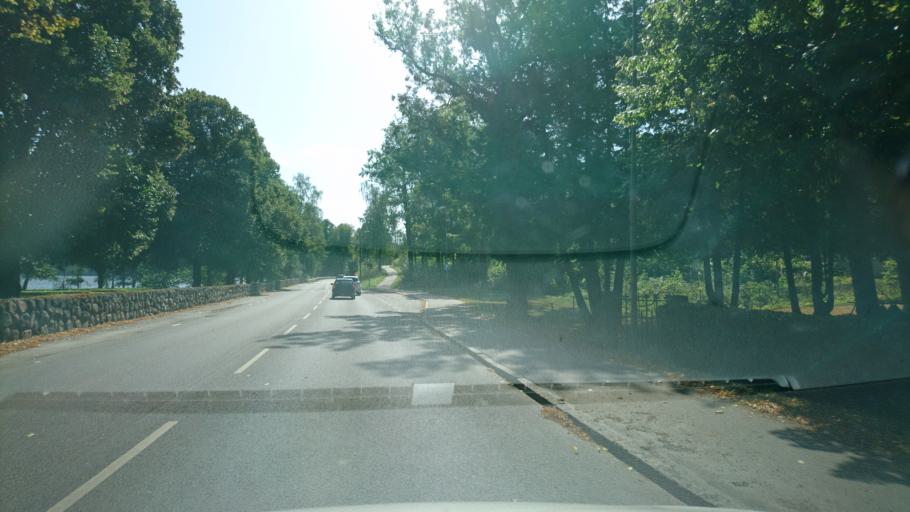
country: SE
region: Soedermanland
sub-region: Strangnas Kommun
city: Strangnas
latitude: 59.3694
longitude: 17.0344
